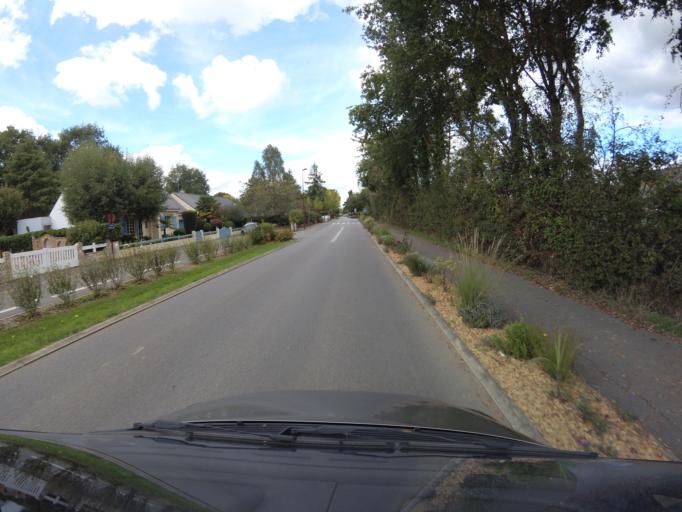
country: FR
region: Pays de la Loire
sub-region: Departement de la Loire-Atlantique
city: Suce-sur-Erdre
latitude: 47.3495
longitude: -1.5358
